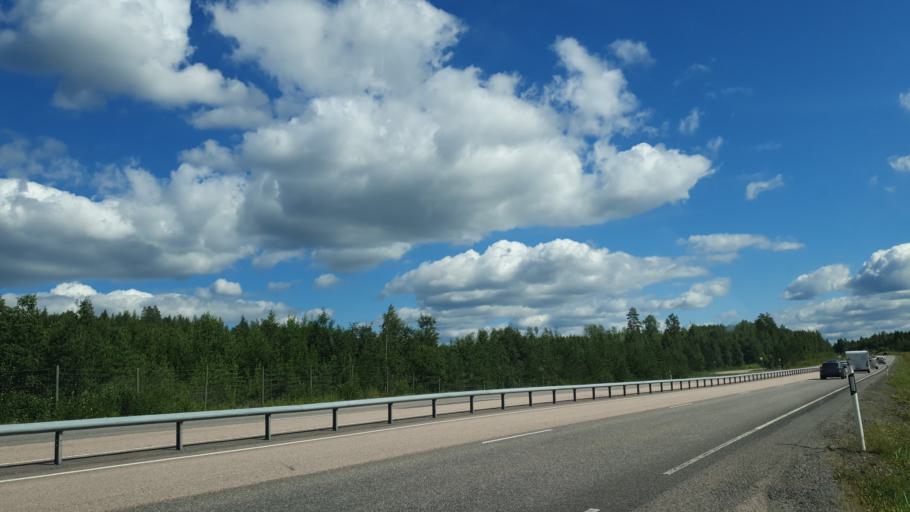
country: FI
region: Pirkanmaa
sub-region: Tampere
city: Orivesi
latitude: 61.7088
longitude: 24.5363
